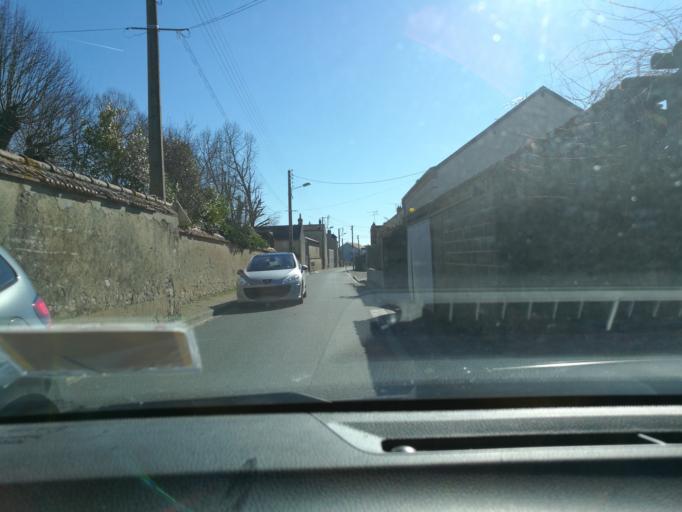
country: FR
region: Centre
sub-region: Departement du Loiret
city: Saint-Jean-le-Blanc
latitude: 47.8836
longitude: 1.9175
